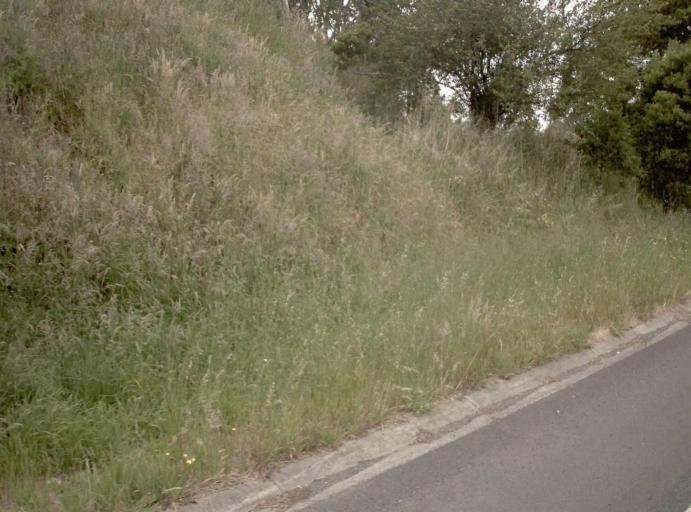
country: AU
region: Victoria
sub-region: Bass Coast
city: North Wonthaggi
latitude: -38.3877
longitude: 145.7457
